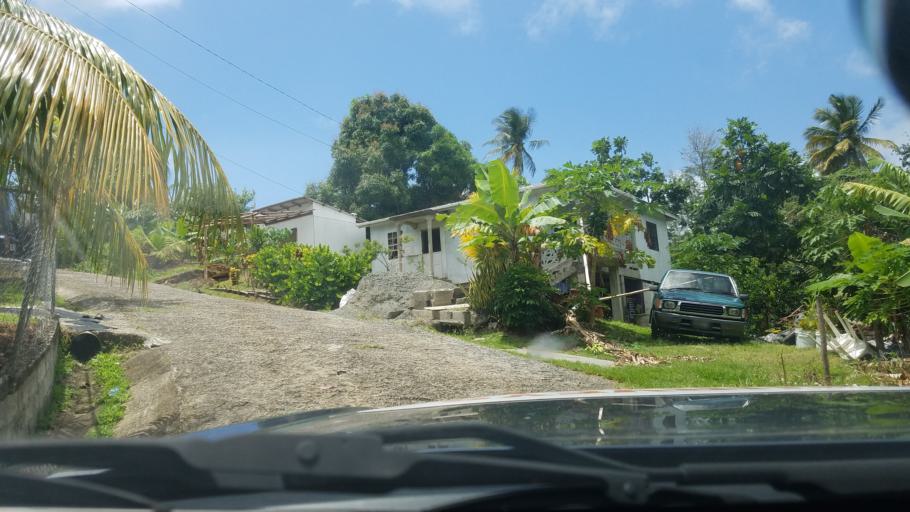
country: LC
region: Gros-Islet
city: Gros Islet
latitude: 14.0598
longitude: -60.9464
